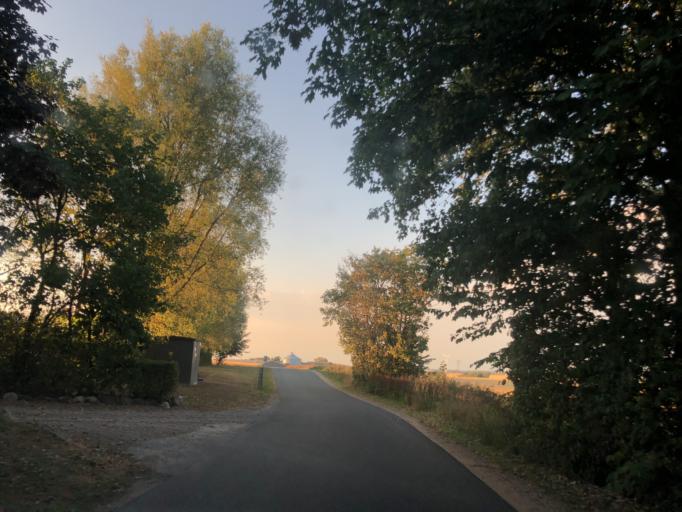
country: DK
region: Central Jutland
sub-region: Holstebro Kommune
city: Holstebro
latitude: 56.3899
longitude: 8.6846
